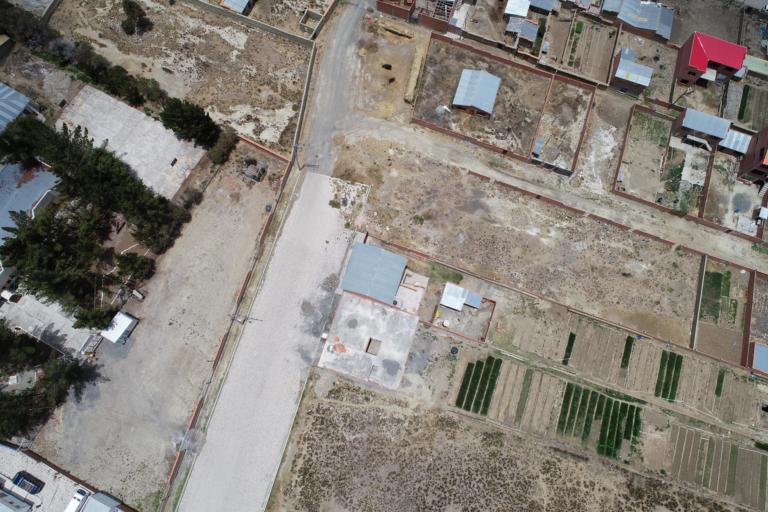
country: BO
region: La Paz
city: Achacachi
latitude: -16.0423
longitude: -68.6919
